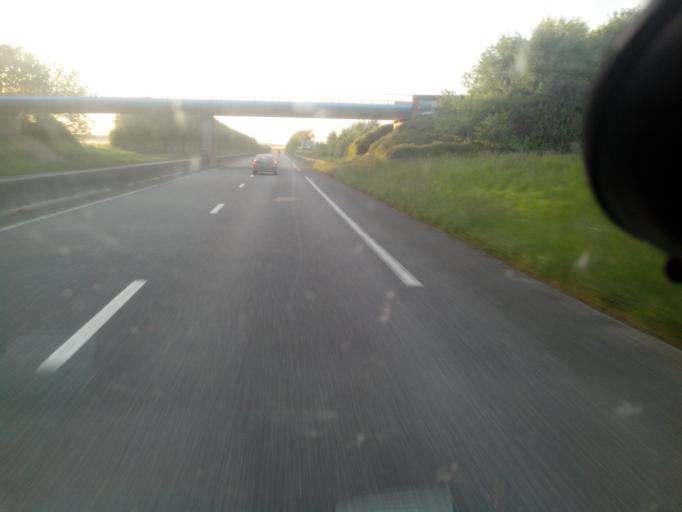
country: FR
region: Picardie
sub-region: Departement de la Somme
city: Abbeville
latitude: 50.0795
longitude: 1.7829
